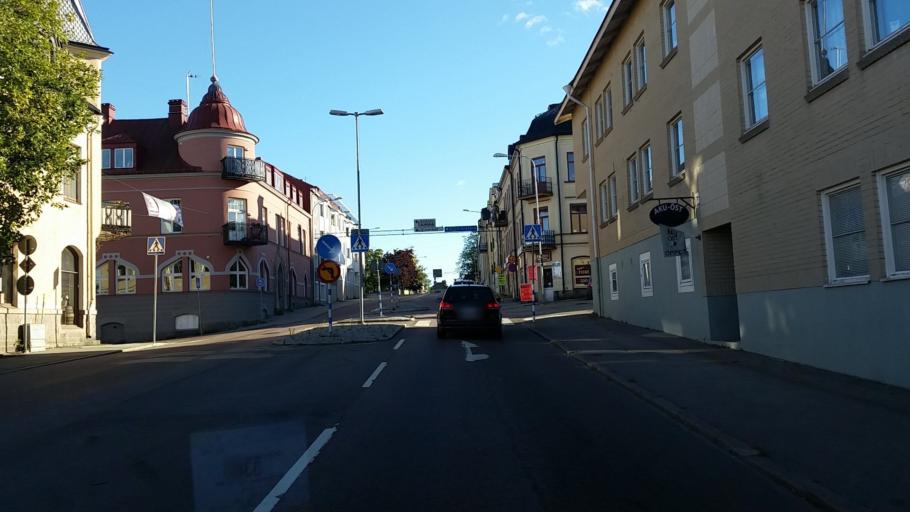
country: SE
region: Gaevleborg
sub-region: Hudiksvalls Kommun
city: Hudiksvall
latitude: 61.7277
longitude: 17.1015
